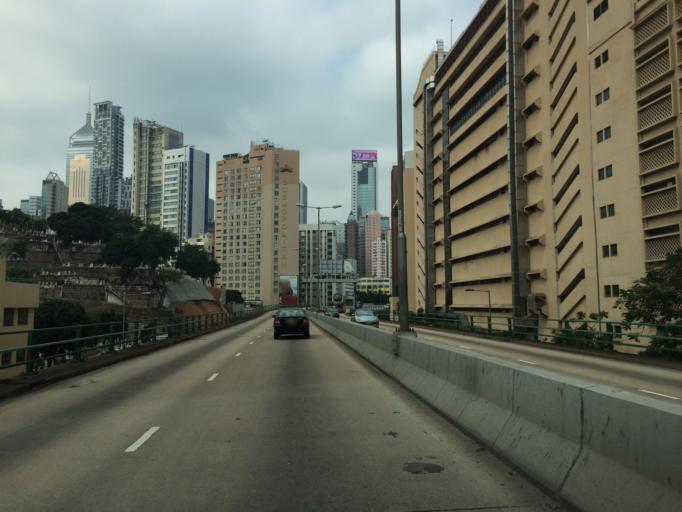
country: HK
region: Wanchai
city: Wan Chai
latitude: 22.2725
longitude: 114.1799
